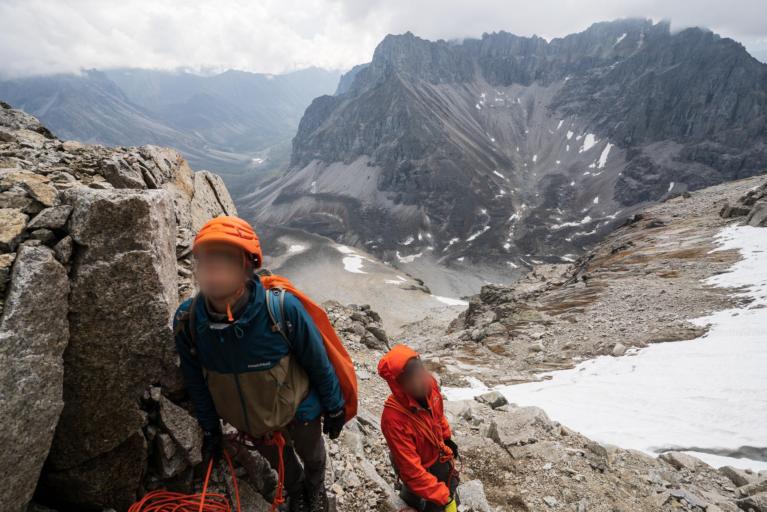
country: RU
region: Transbaikal Territory
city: Chara
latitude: 56.8657
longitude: 117.5804
